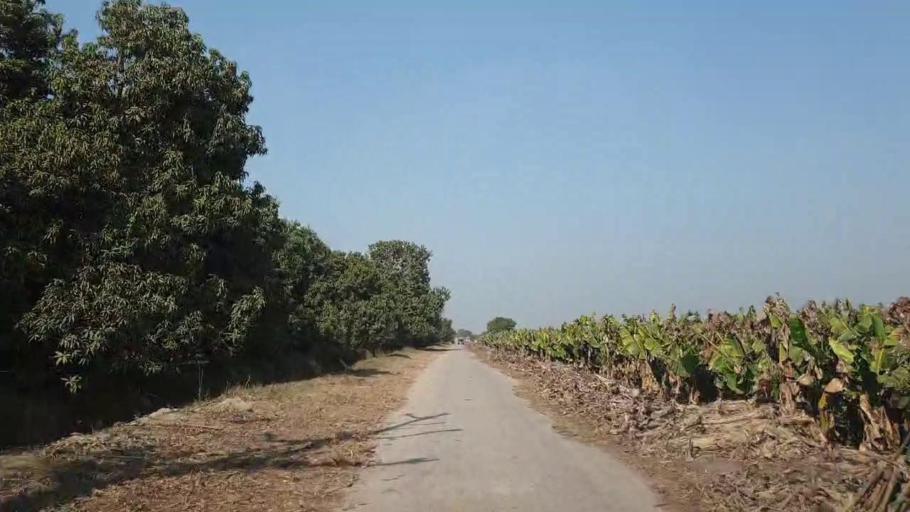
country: PK
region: Sindh
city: Tando Allahyar
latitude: 25.5039
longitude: 68.8221
